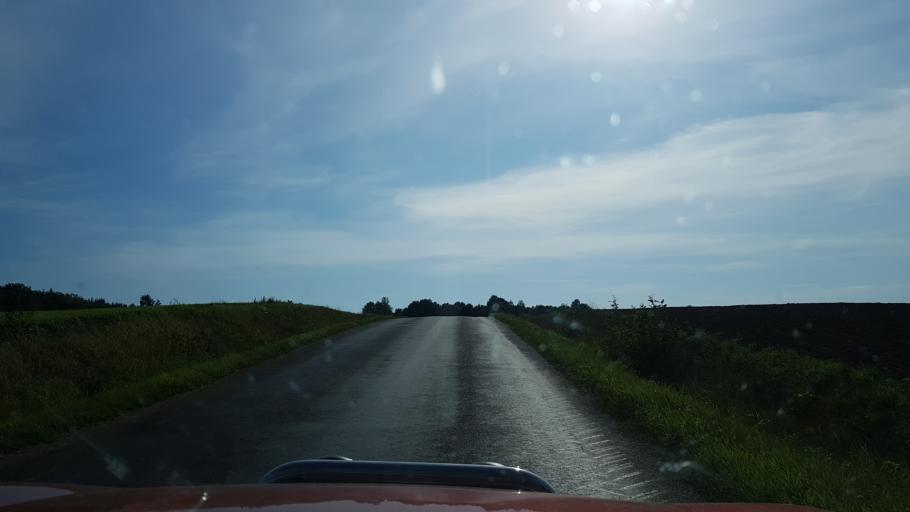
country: EE
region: Viljandimaa
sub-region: Viiratsi vald
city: Viiratsi
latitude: 58.2654
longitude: 25.6208
